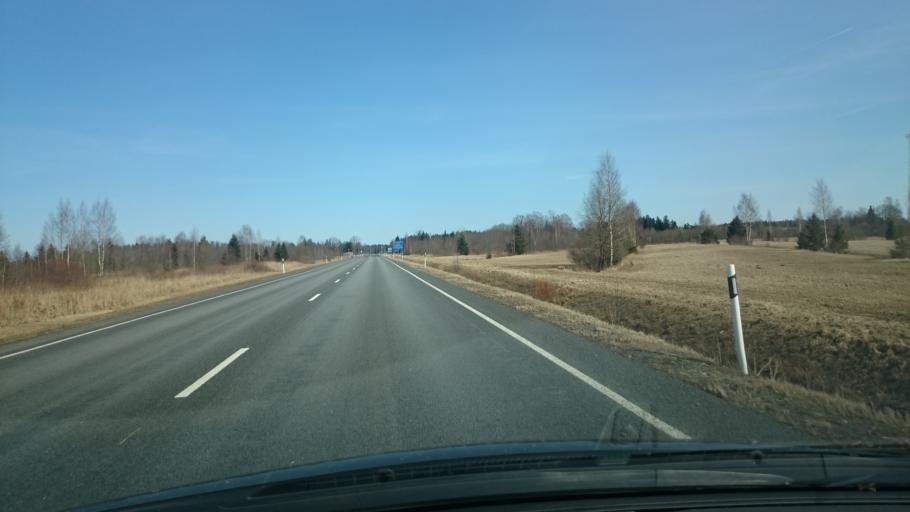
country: EE
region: Paernumaa
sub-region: Vaendra vald (alev)
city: Vandra
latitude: 58.6601
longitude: 25.0151
